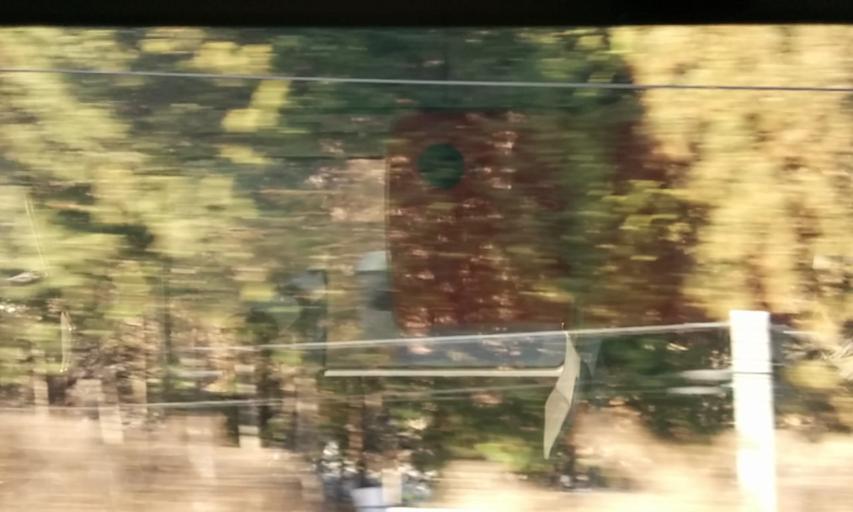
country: JP
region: Nagano
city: Ina
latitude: 35.8687
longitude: 137.7325
